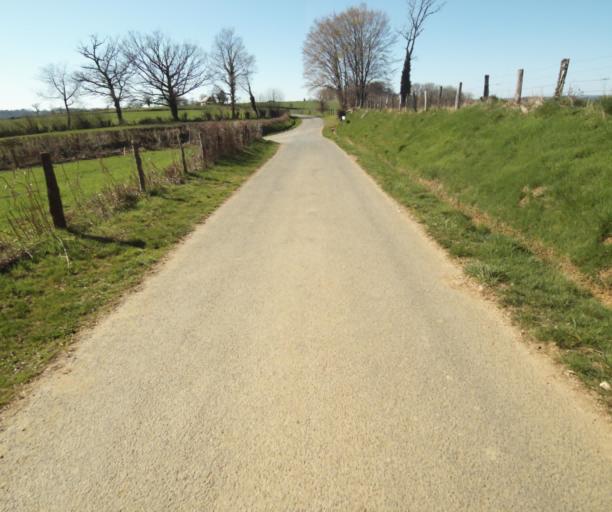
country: FR
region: Limousin
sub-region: Departement de la Correze
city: Uzerche
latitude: 45.4148
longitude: 1.6305
